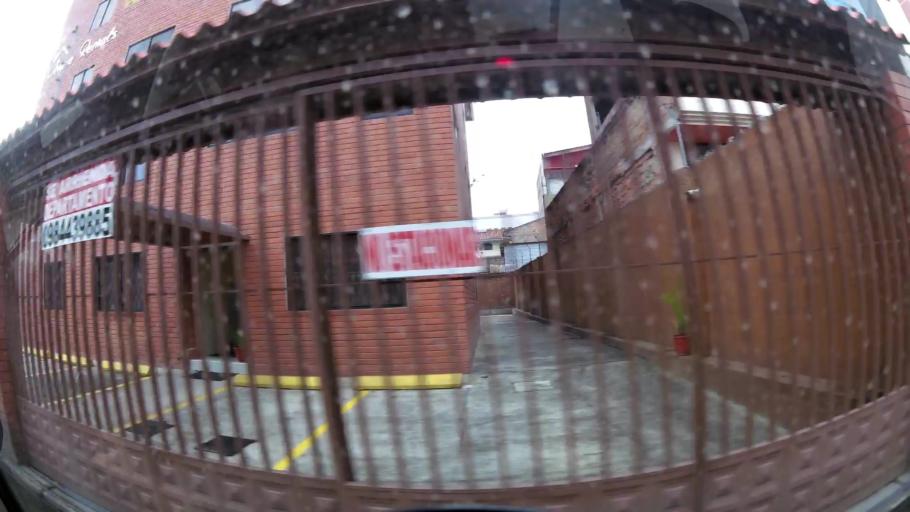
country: EC
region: Azuay
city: Cuenca
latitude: -2.8998
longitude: -79.0248
